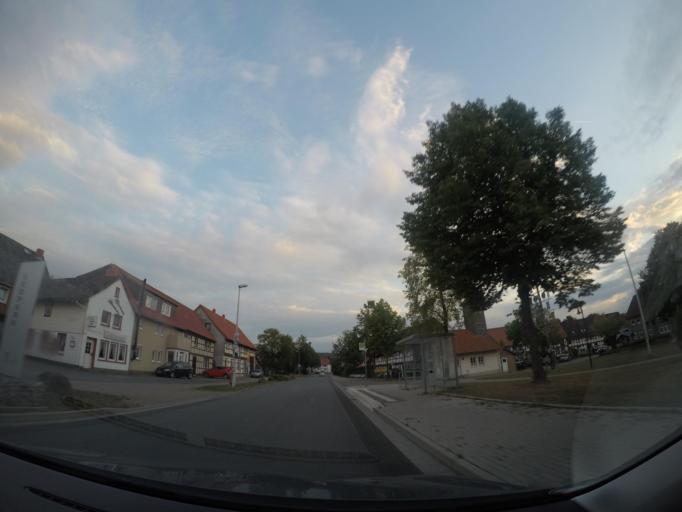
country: DE
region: Lower Saxony
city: Seesen
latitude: 51.8500
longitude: 10.1803
